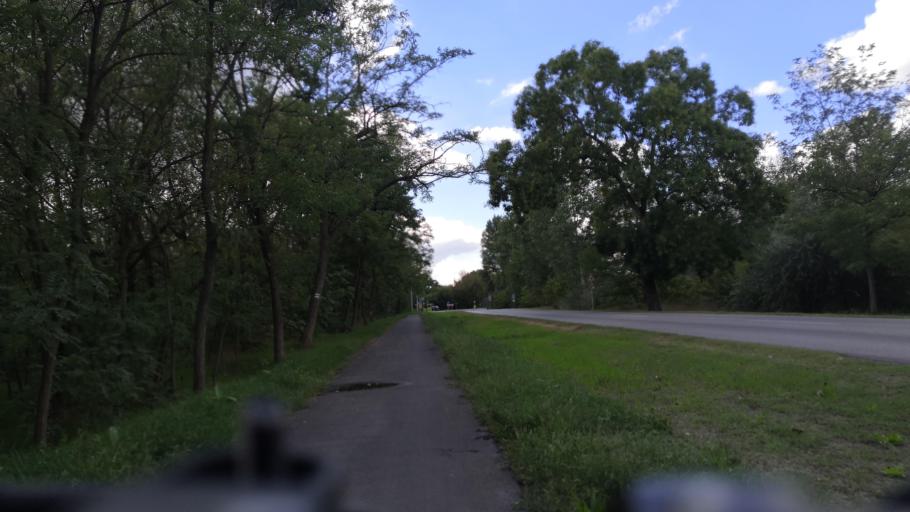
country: HU
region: Csongrad
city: Domaszek
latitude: 46.2744
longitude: 20.0266
